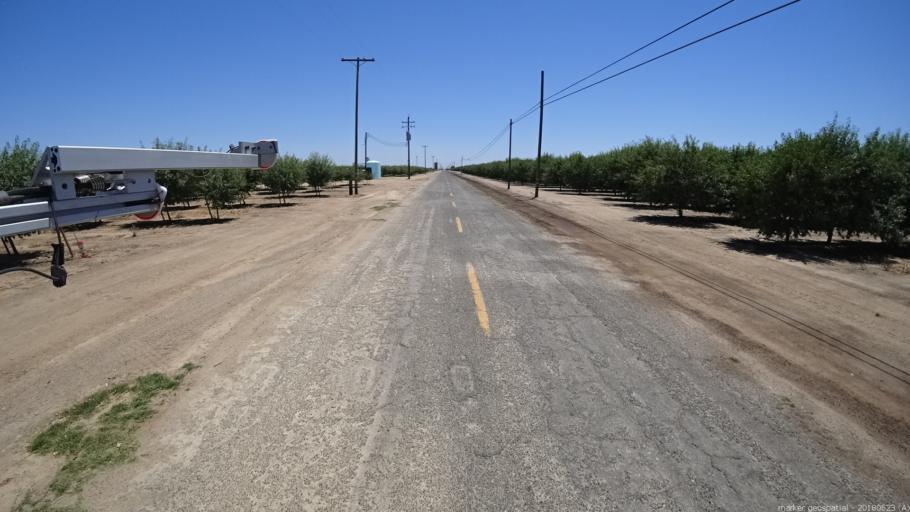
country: US
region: California
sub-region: Madera County
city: Chowchilla
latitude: 37.0911
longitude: -120.2411
